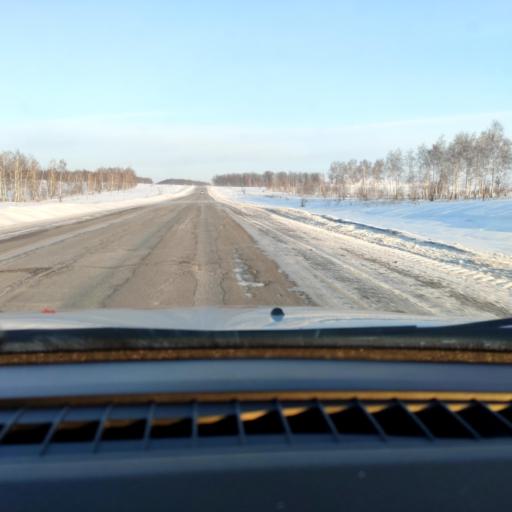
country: RU
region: Samara
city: Kinel'
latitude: 53.4417
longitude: 50.6178
